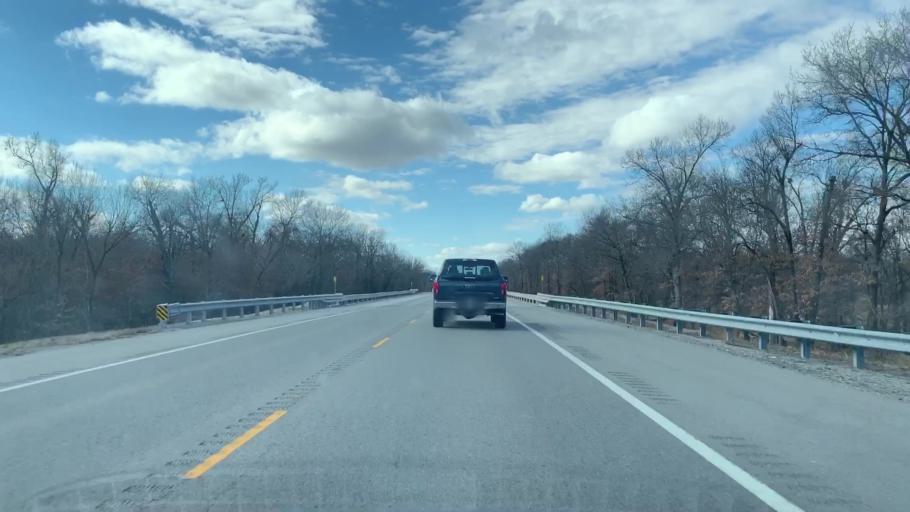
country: US
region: Kansas
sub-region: Cherokee County
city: Columbus
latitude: 37.3401
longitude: -94.9707
